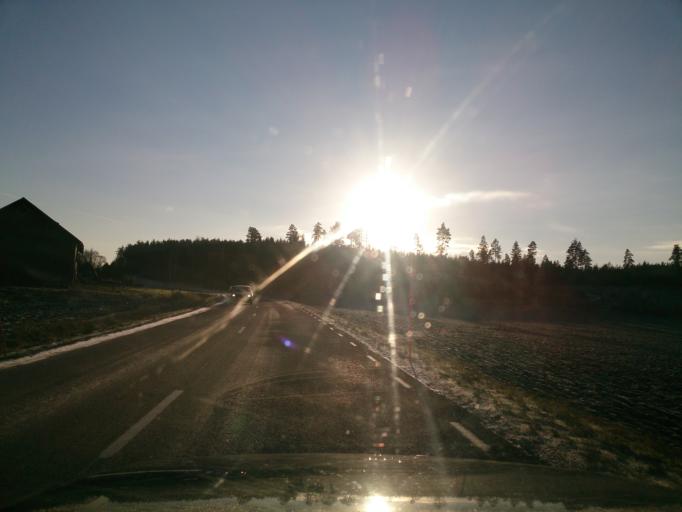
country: SE
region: OEstergoetland
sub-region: Linkopings Kommun
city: Linghem
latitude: 58.4442
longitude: 15.8884
